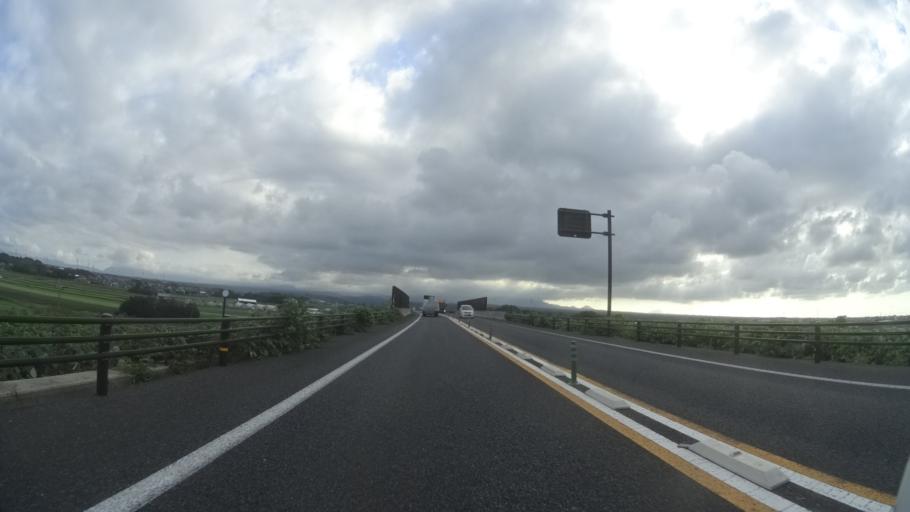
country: JP
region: Tottori
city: Kurayoshi
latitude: 35.4972
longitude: 133.7132
